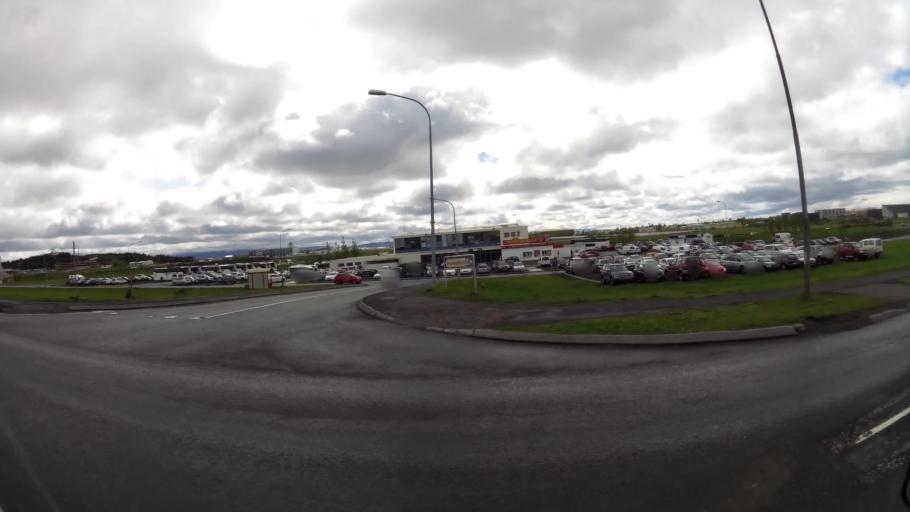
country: IS
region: Capital Region
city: Kopavogur
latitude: 64.1385
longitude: -21.9341
